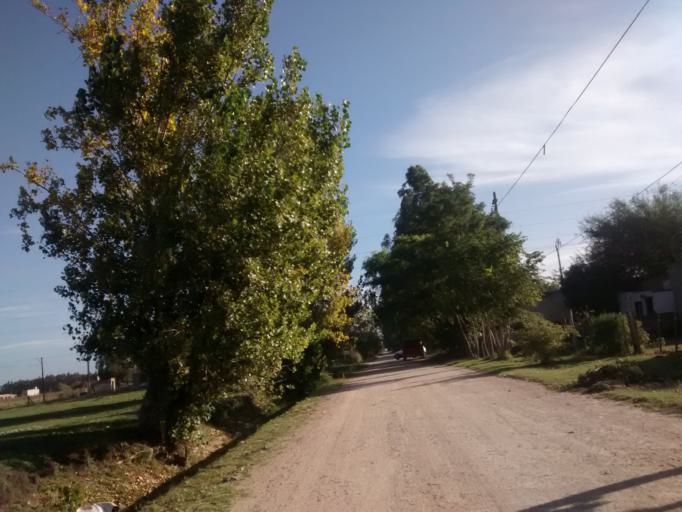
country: AR
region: Buenos Aires
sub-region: Partido de Loberia
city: Loberia
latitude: -38.1713
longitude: -58.7851
